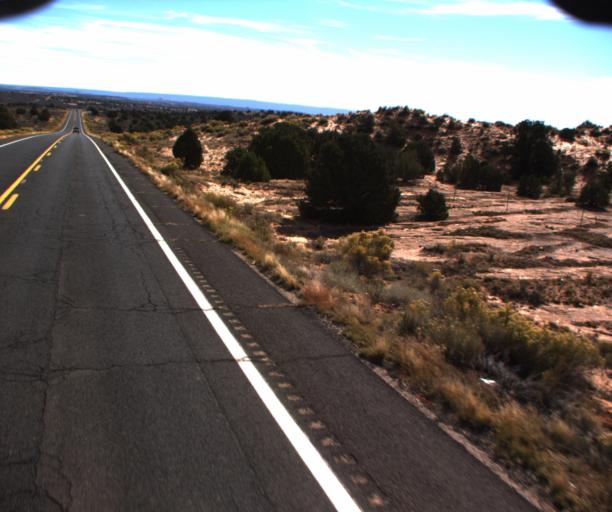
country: US
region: Arizona
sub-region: Coconino County
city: Kaibito
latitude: 36.5796
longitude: -110.7892
